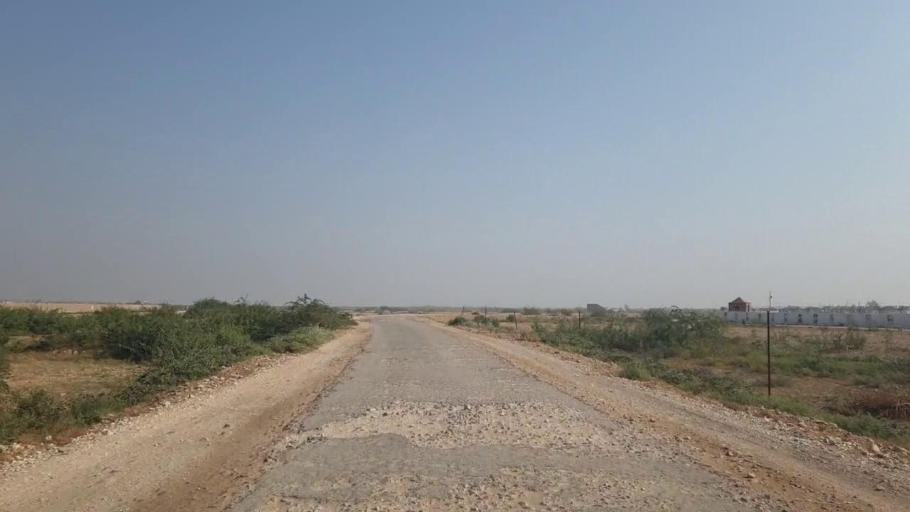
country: PK
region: Sindh
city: Jamshoro
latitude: 25.5356
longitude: 68.3360
